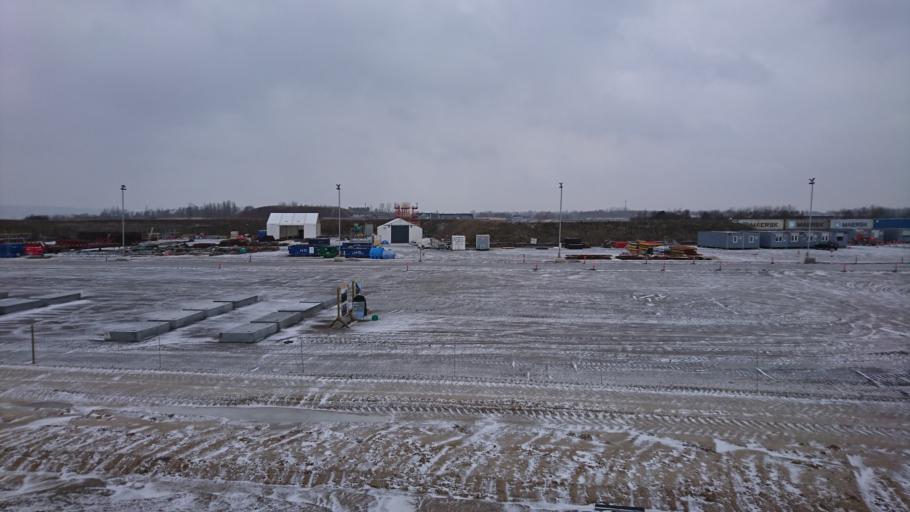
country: DK
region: Capital Region
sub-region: Frederikssund Kommune
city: Frederikssund
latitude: 55.8134
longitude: 12.0741
